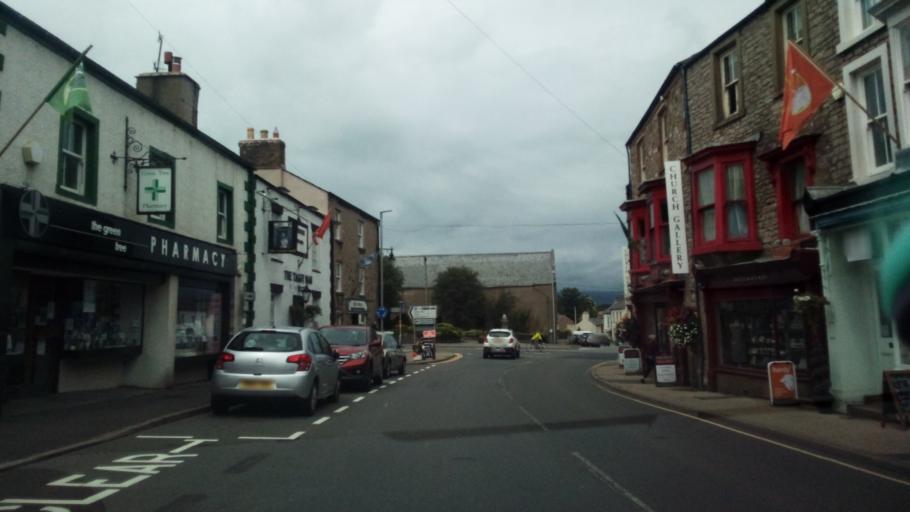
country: GB
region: England
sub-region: Cumbria
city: Kirkby Stephen
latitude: 54.4740
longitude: -2.3491
